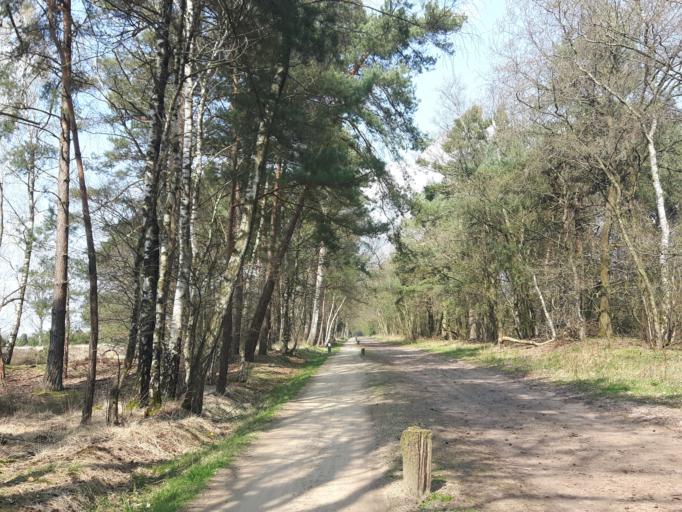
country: NL
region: Overijssel
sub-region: Gemeente Haaksbergen
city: Haaksbergen
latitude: 52.1620
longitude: 6.8095
